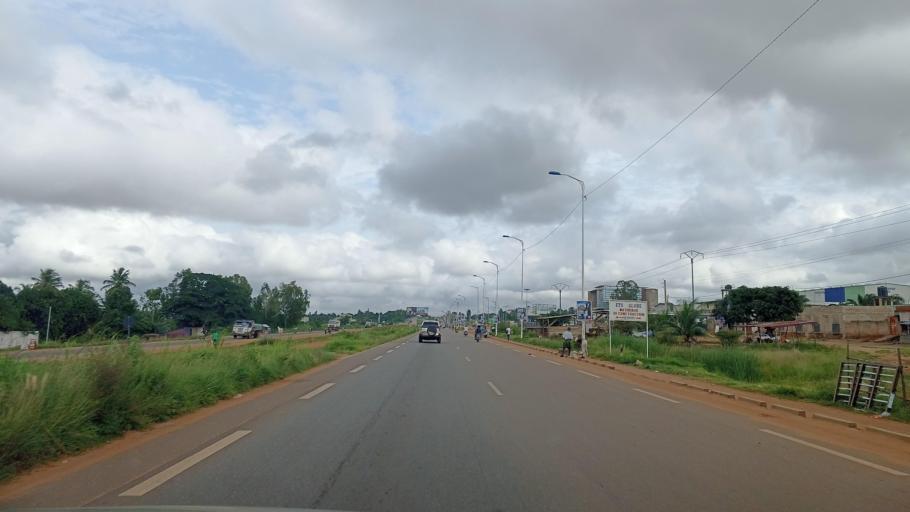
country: TG
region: Maritime
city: Tsevie
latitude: 6.3308
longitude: 1.2179
